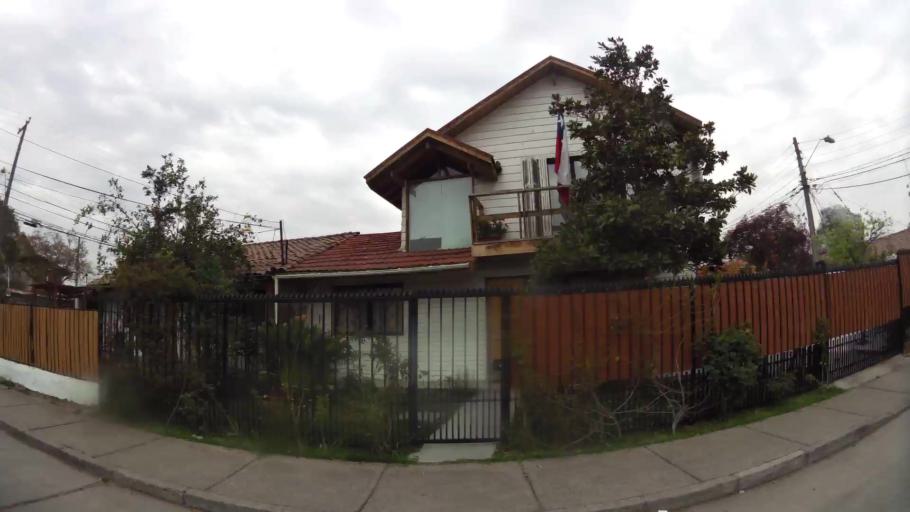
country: CL
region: Santiago Metropolitan
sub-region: Provincia de Santiago
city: Villa Presidente Frei, Nunoa, Santiago, Chile
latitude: -33.5130
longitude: -70.6031
